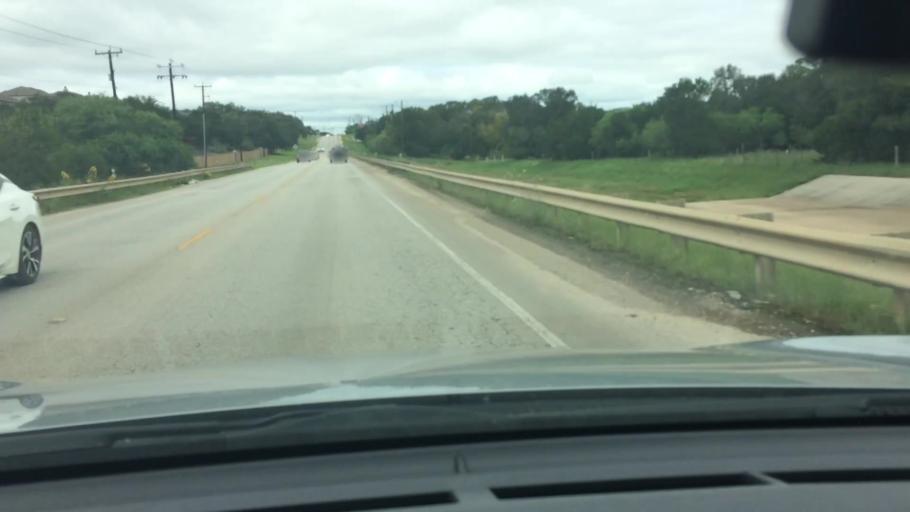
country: US
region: Texas
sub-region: Comal County
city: Garden Ridge
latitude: 29.6438
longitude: -98.3949
